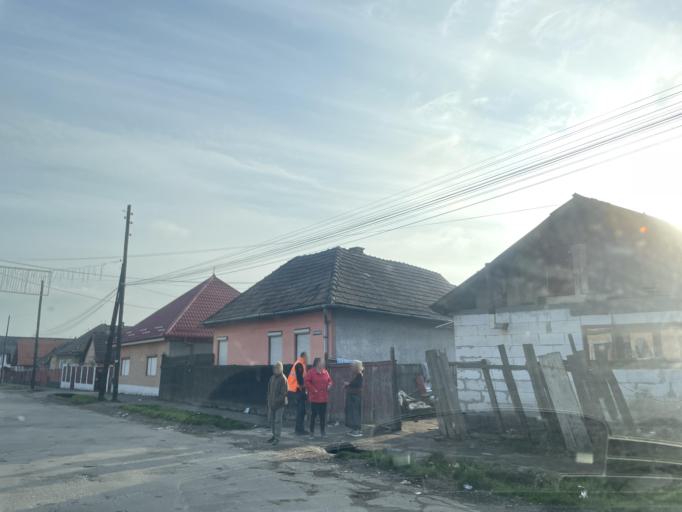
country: RO
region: Mures
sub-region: Municipiul Reghin
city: Apalina
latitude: 46.7594
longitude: 24.6901
